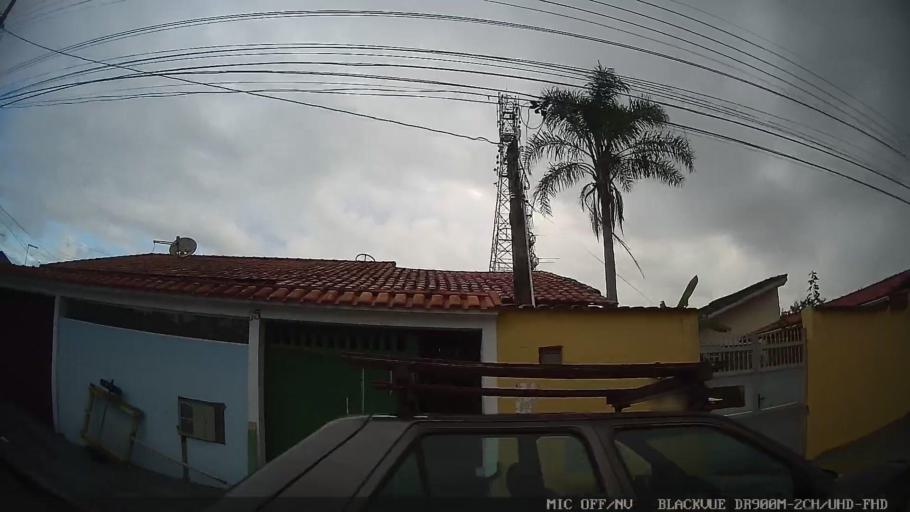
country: BR
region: Sao Paulo
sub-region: Itanhaem
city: Itanhaem
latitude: -24.1772
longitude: -46.7910
